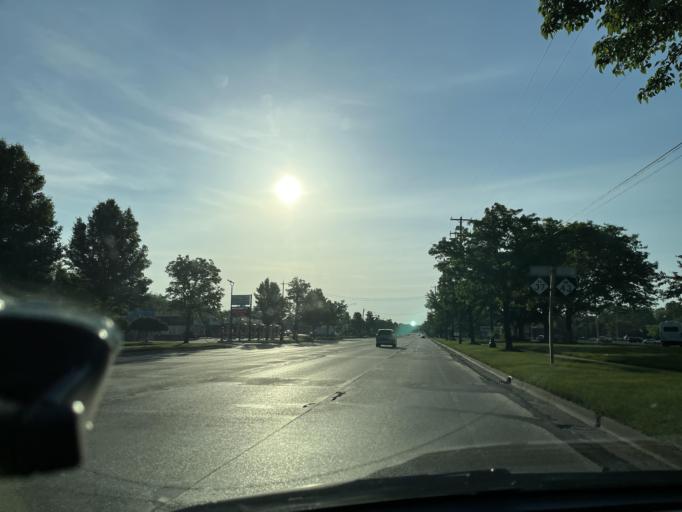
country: US
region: Michigan
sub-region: Barry County
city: Hastings
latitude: 42.6486
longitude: -85.2994
